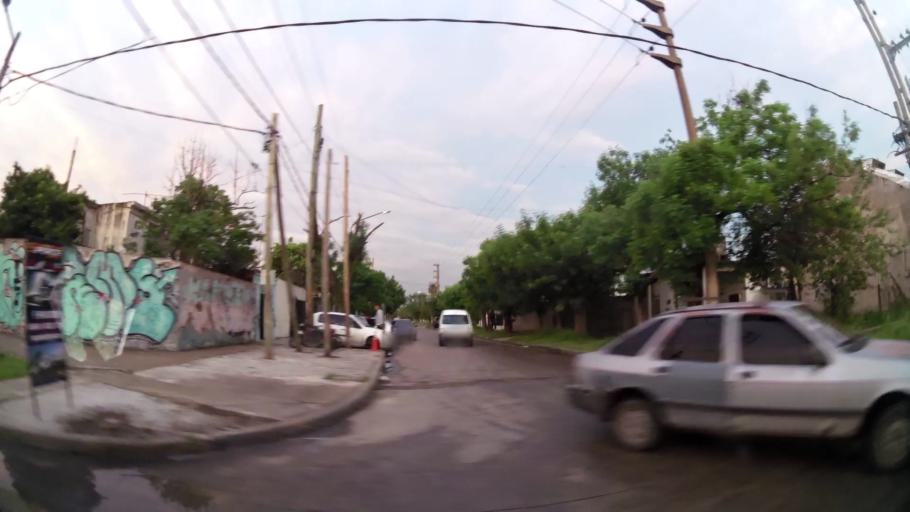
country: AR
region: Buenos Aires
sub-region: Partido de Lomas de Zamora
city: Lomas de Zamora
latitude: -34.7504
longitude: -58.3630
